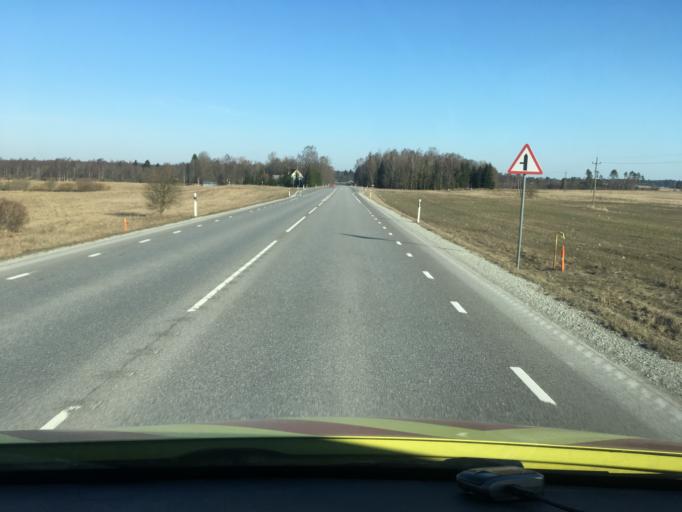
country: EE
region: Harju
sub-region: Saku vald
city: Saku
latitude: 59.2875
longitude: 24.7401
